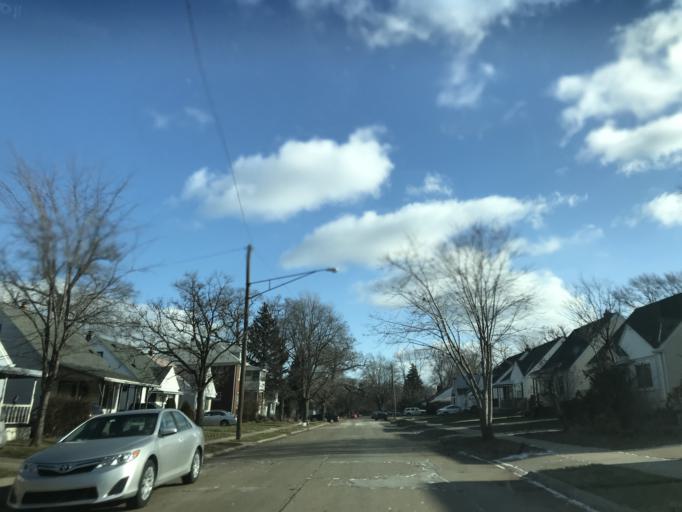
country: US
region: Michigan
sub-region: Oakland County
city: Hazel Park
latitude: 42.4584
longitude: -83.0984
